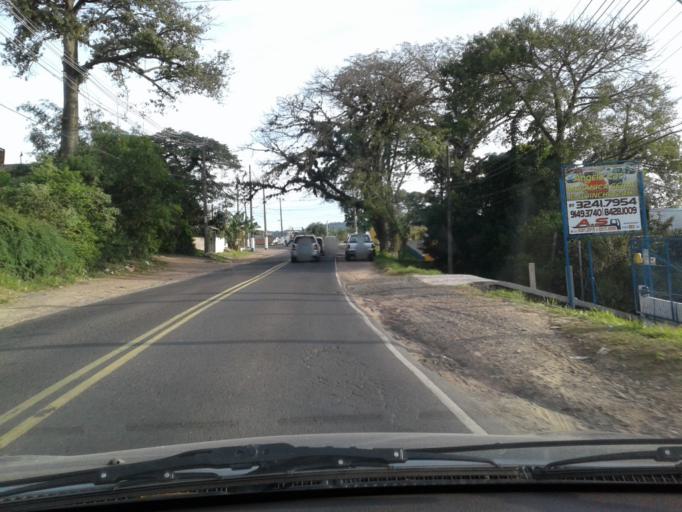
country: BR
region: Rio Grande do Sul
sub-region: Porto Alegre
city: Porto Alegre
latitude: -30.0977
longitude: -51.2248
